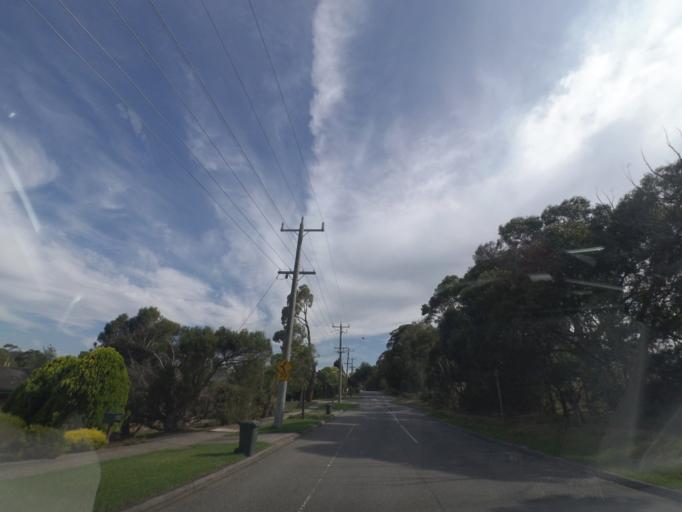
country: AU
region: Victoria
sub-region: Banyule
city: Viewbank
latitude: -37.7424
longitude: 145.0960
